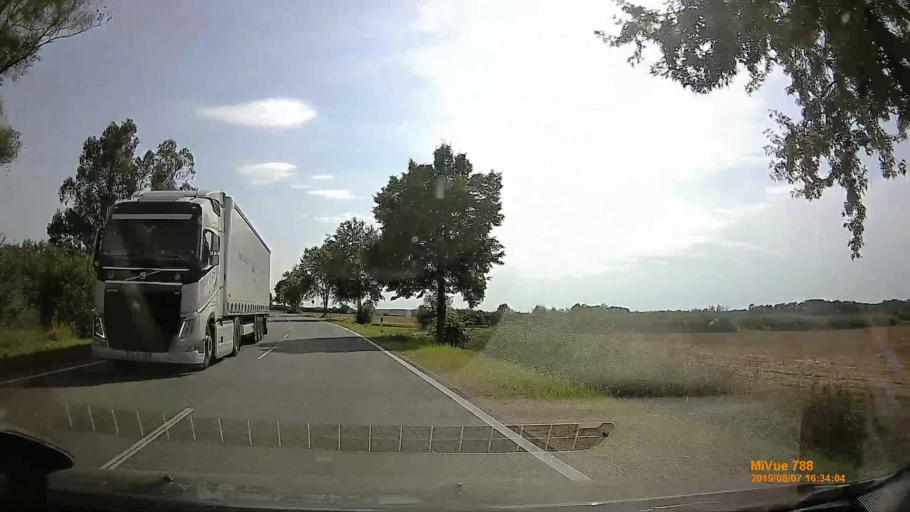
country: SI
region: Lendava-Lendva
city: Lendava
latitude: 46.6262
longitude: 16.4689
